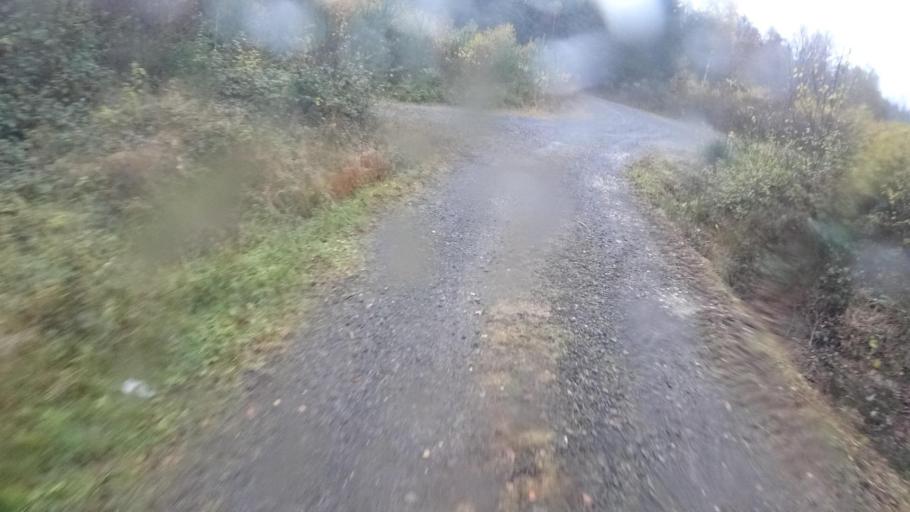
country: DE
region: Rheinland-Pfalz
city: Maisborn
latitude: 50.0915
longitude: 7.5855
